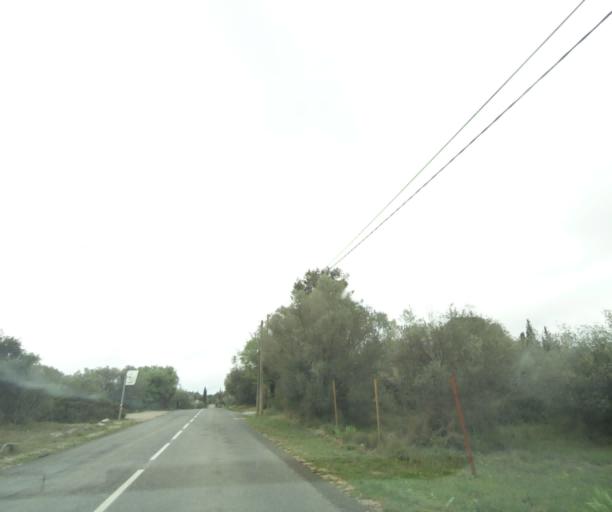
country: FR
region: Languedoc-Roussillon
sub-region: Departement de l'Herault
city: Pignan
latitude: 43.5932
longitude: 3.7502
